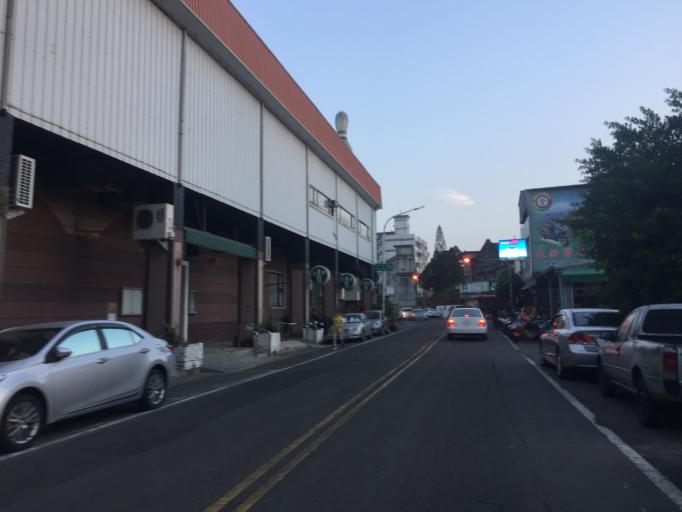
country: TW
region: Taiwan
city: Xinying
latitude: 23.3065
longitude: 120.3202
